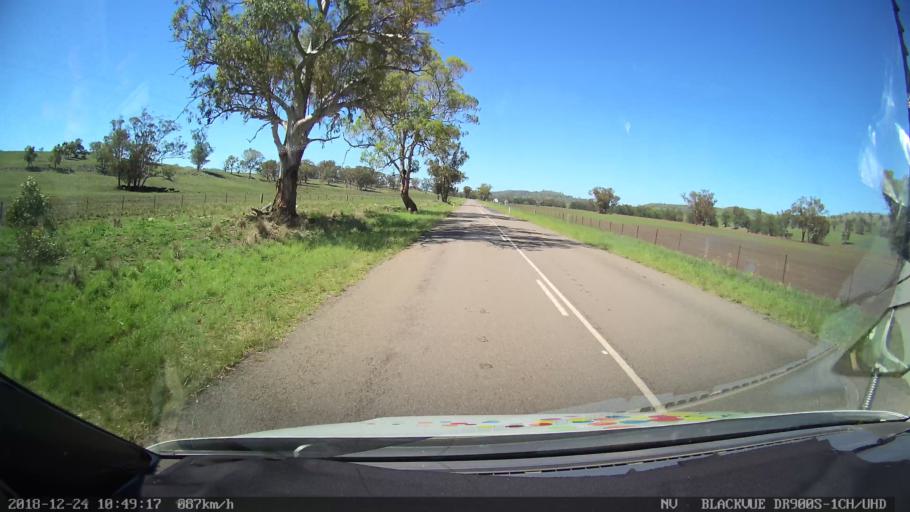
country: AU
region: New South Wales
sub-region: Upper Hunter Shire
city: Merriwa
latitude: -31.9456
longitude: 150.4282
